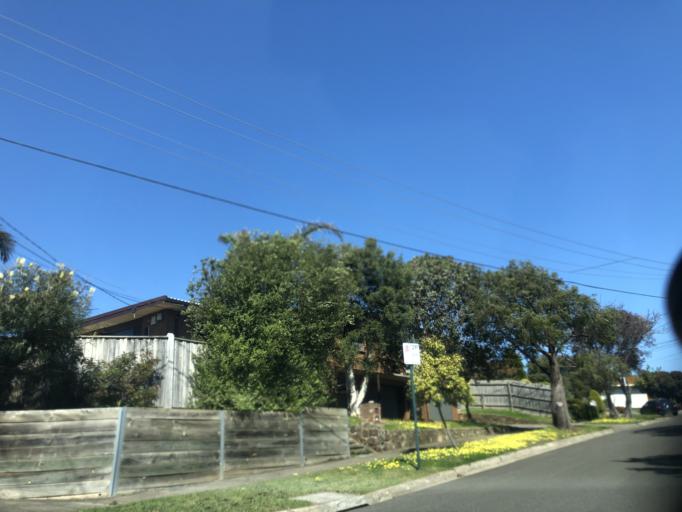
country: AU
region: Victoria
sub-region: Monash
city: Notting Hill
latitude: -37.8924
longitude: 145.1391
